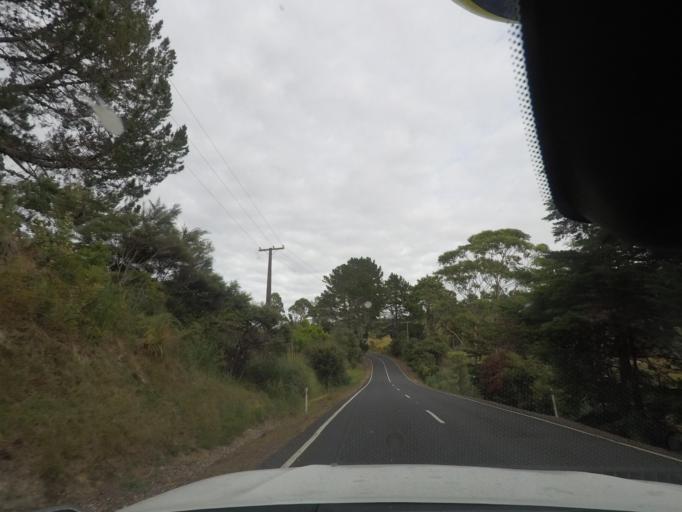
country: NZ
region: Auckland
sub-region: Auckland
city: Parakai
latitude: -36.5215
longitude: 174.2788
